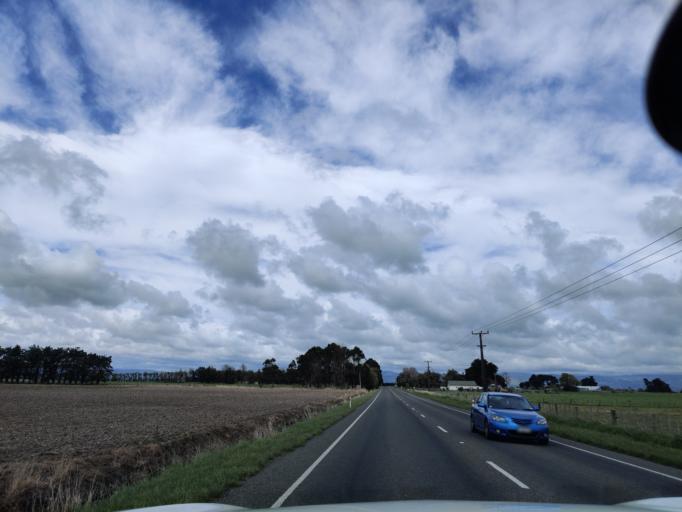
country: NZ
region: Manawatu-Wanganui
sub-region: Palmerston North City
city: Palmerston North
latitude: -40.3237
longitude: 175.5030
